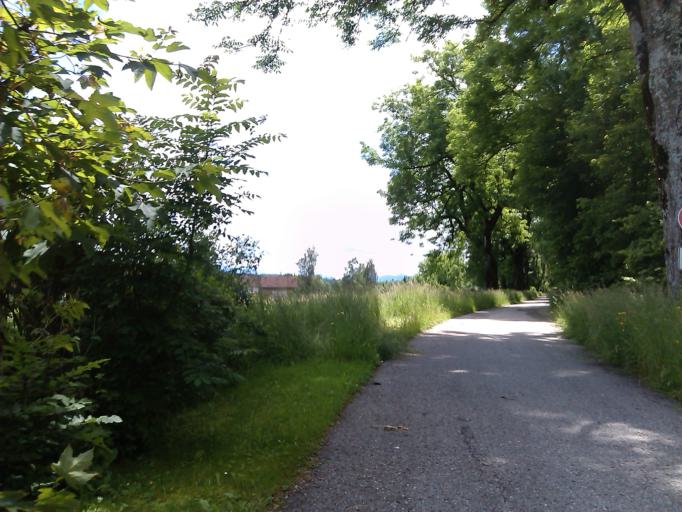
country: DE
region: Bavaria
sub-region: Swabia
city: Kaufbeuren
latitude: 47.8612
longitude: 10.6306
